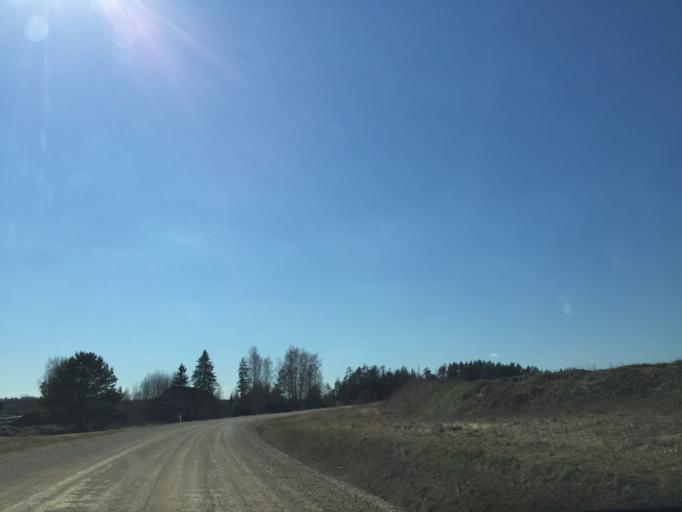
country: EE
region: Viljandimaa
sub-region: Viiratsi vald
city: Viiratsi
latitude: 58.3068
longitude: 25.6466
